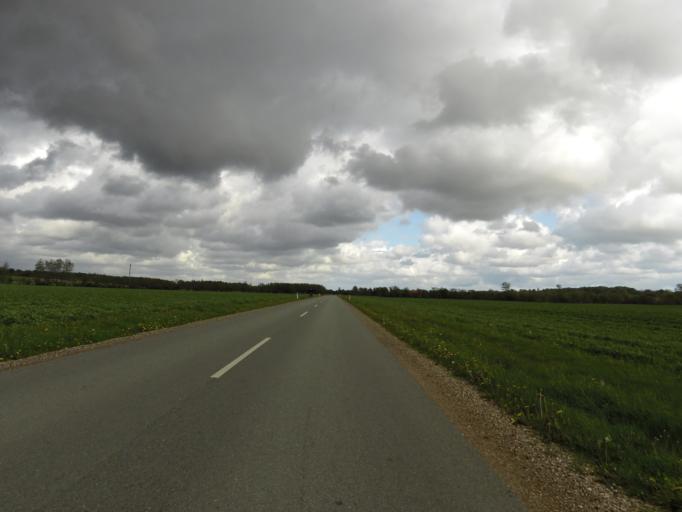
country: DK
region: South Denmark
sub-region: Haderslev Kommune
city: Gram
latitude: 55.3011
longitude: 9.0433
